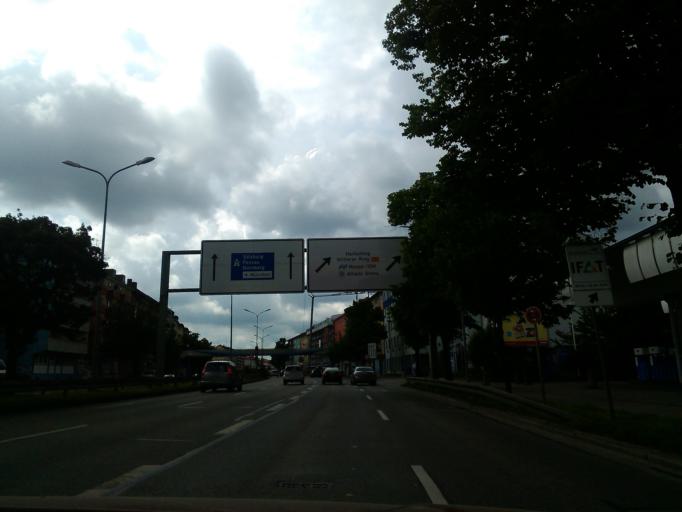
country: DE
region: Bavaria
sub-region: Upper Bavaria
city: Munich
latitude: 48.1078
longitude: 11.5796
